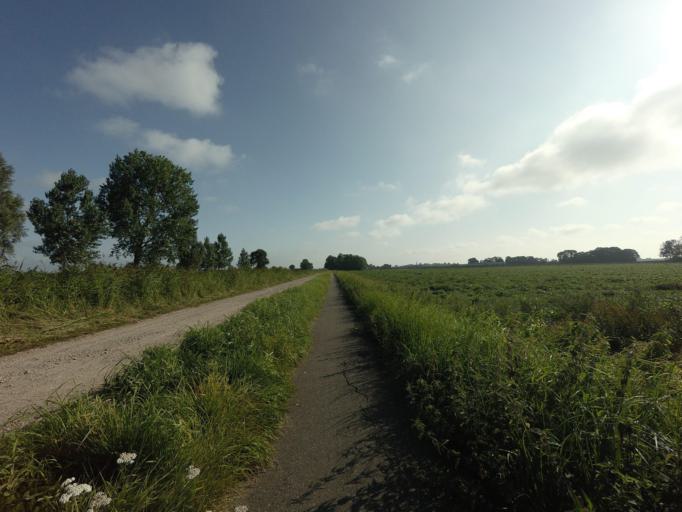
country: NL
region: Overijssel
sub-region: Gemeente Steenwijkerland
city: Steenwijkerwold
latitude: 52.7796
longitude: 6.0672
